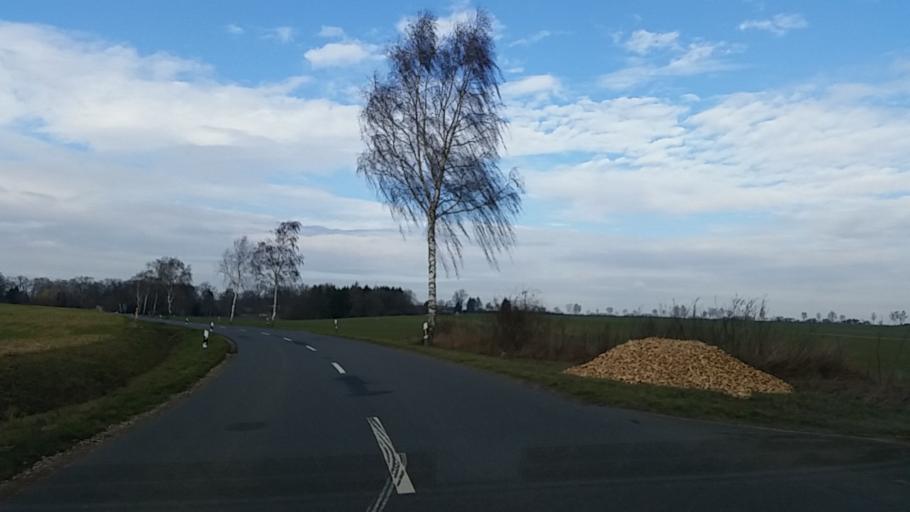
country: DE
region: Lower Saxony
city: Romstedt
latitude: 53.1139
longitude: 10.6467
